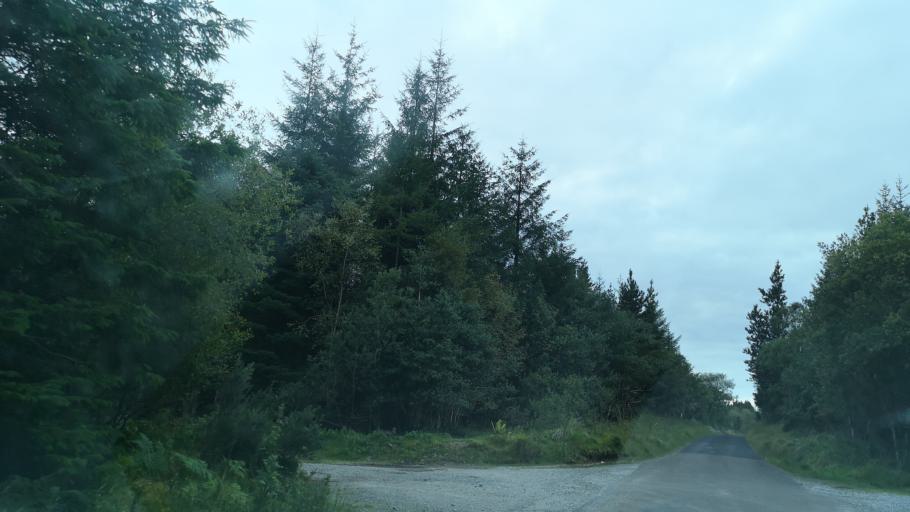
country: IE
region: Connaught
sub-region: County Galway
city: Loughrea
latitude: 53.1330
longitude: -8.5038
